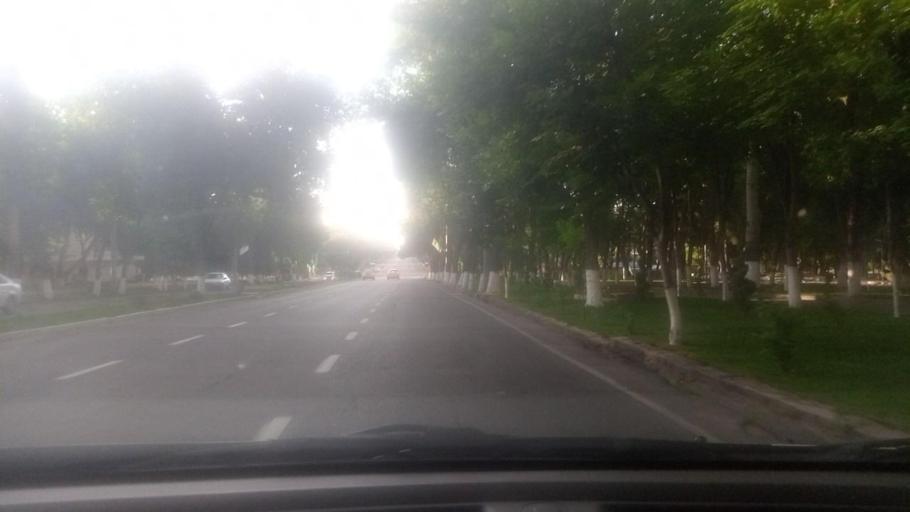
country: UZ
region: Toshkent
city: Salor
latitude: 41.3395
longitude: 69.3373
